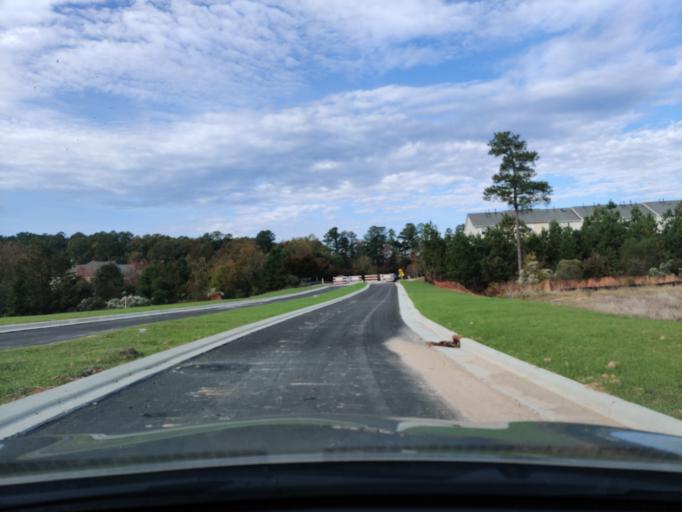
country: US
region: North Carolina
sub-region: Wake County
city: Morrisville
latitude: 35.8279
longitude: -78.8585
